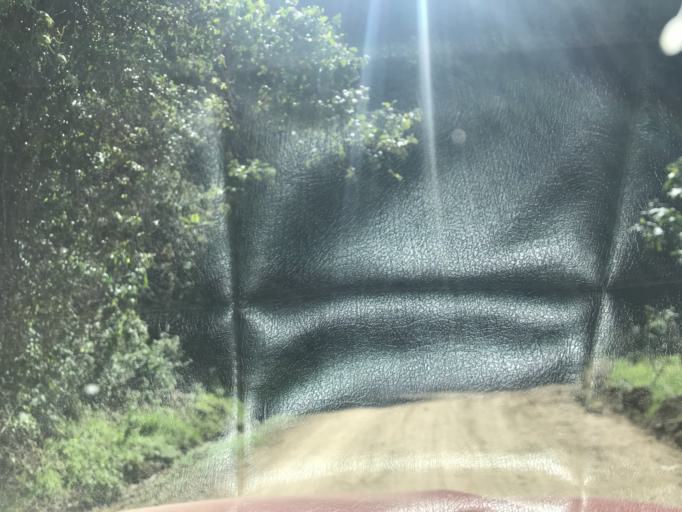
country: PE
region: Cajamarca
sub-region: Provincia de Chota
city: Querocoto
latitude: -6.3524
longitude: -79.0459
